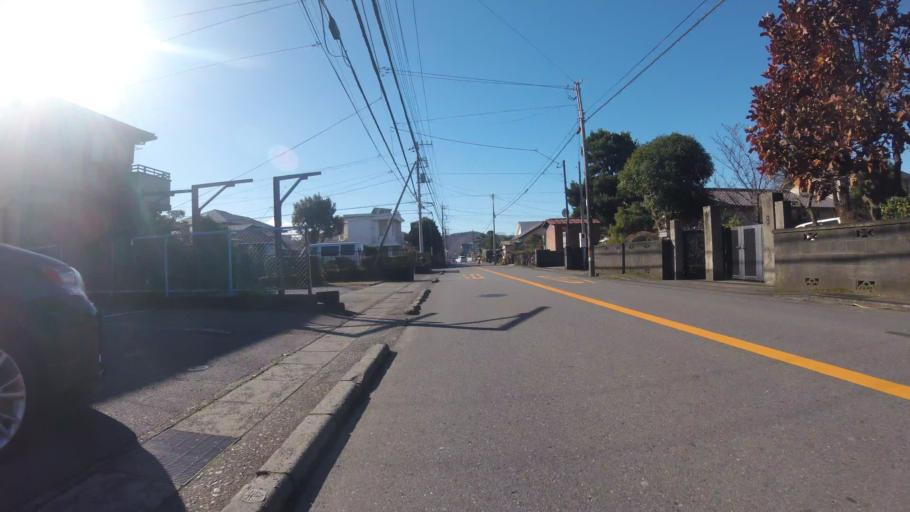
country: JP
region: Shizuoka
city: Mishima
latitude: 35.1116
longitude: 138.8992
